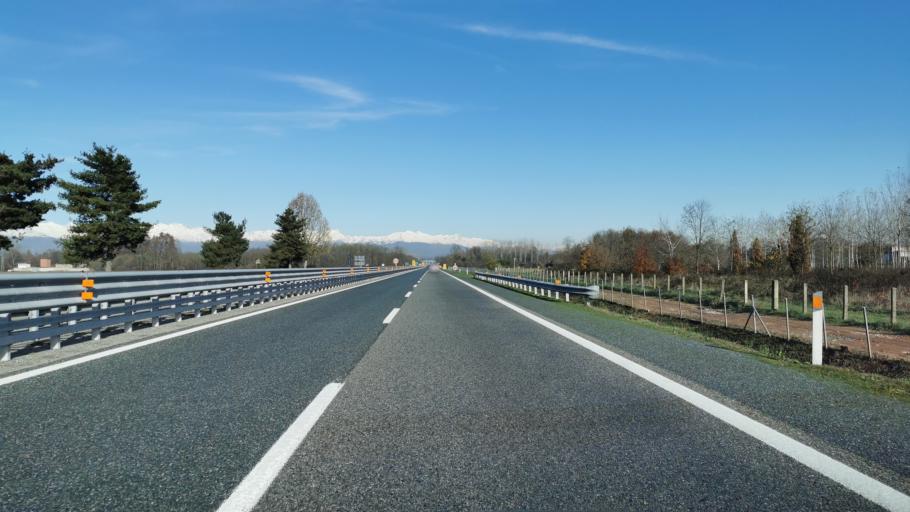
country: IT
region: Piedmont
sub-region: Provincia di Torino
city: Volpiano
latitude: 45.2034
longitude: 7.7947
